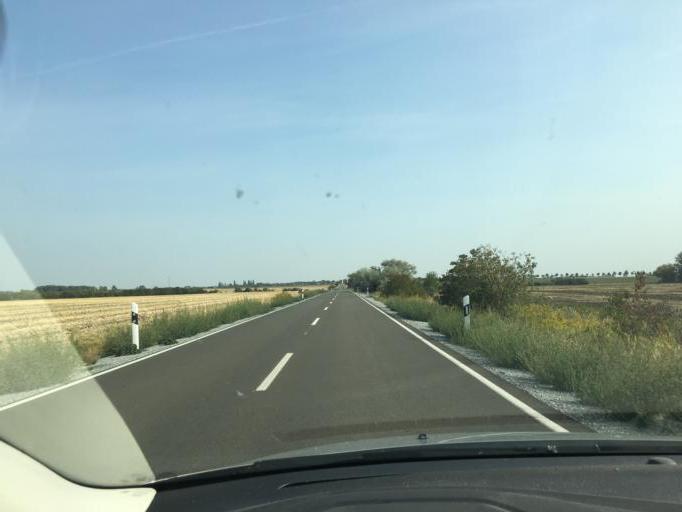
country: DE
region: Saxony-Anhalt
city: Baalberge
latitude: 51.8000
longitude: 11.8574
